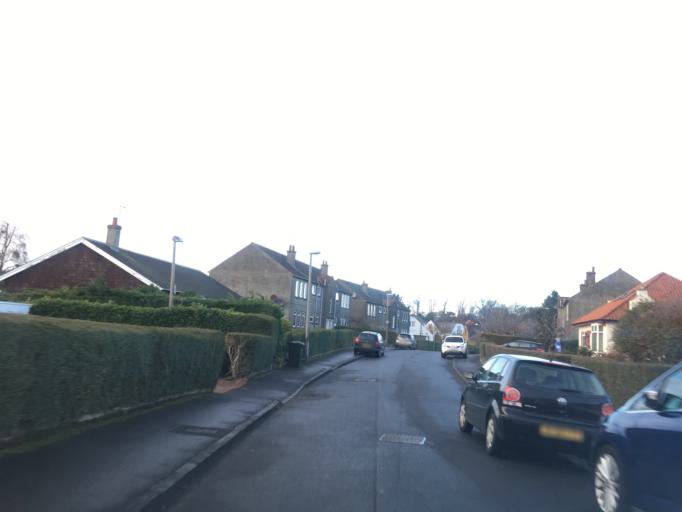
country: GB
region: Scotland
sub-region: Edinburgh
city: Colinton
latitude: 55.9680
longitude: -3.2713
